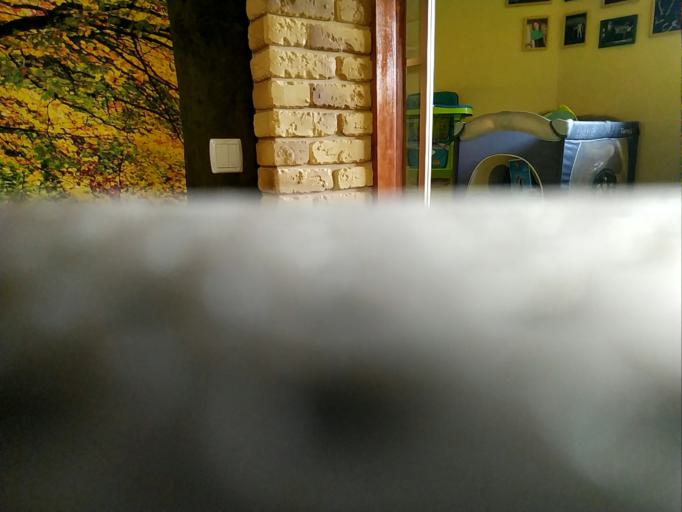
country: RU
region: Kaluga
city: Sukhinichi
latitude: 54.0942
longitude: 35.2817
